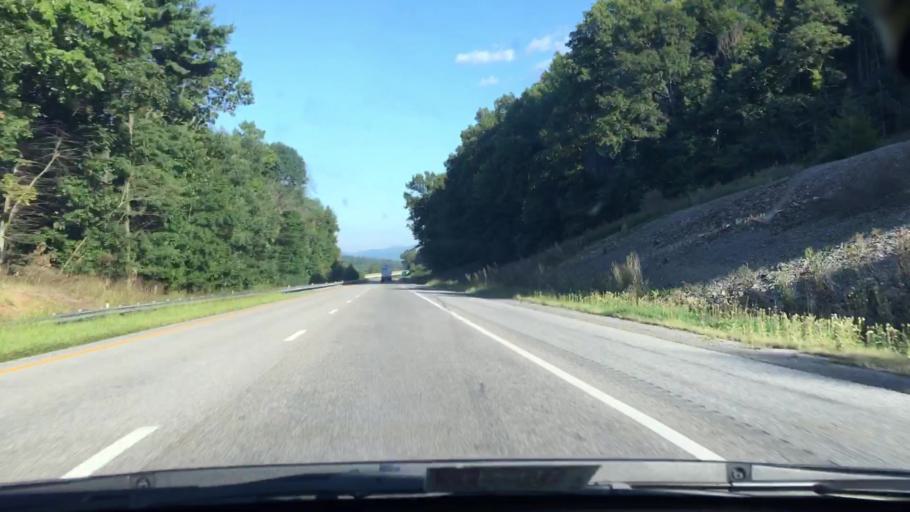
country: US
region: Virginia
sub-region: City of Lexington
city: Lexington
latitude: 37.8666
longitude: -79.5019
